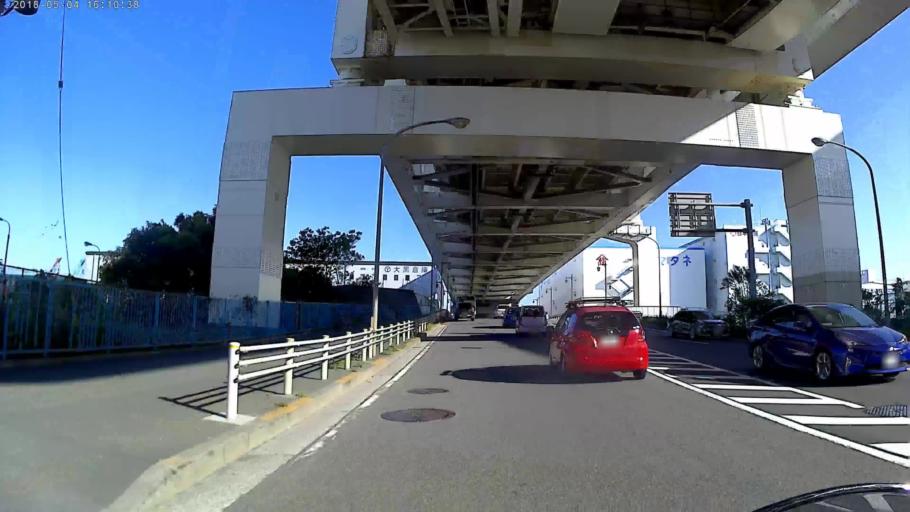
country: JP
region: Kanagawa
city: Yokohama
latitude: 35.4905
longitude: 139.6716
